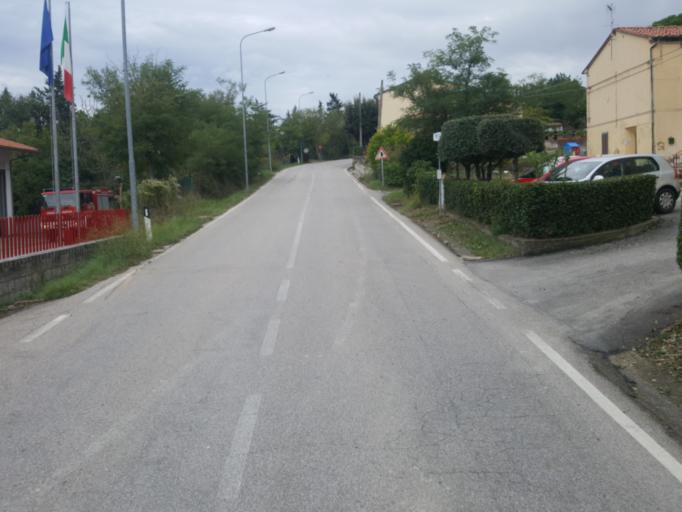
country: IT
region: Tuscany
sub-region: Province of Pisa
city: Saline
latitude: 43.3572
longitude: 10.8129
